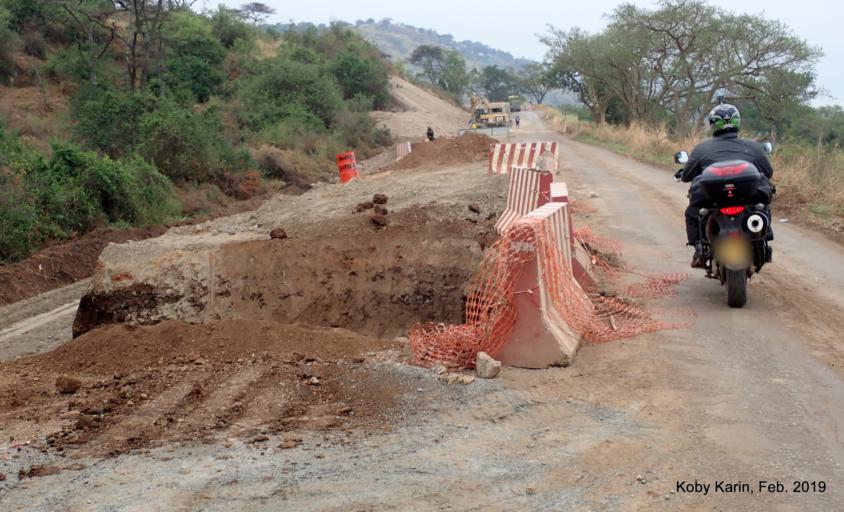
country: UG
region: Western Region
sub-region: Rubirizi District
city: Rubirizi
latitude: -0.2128
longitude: 30.0933
